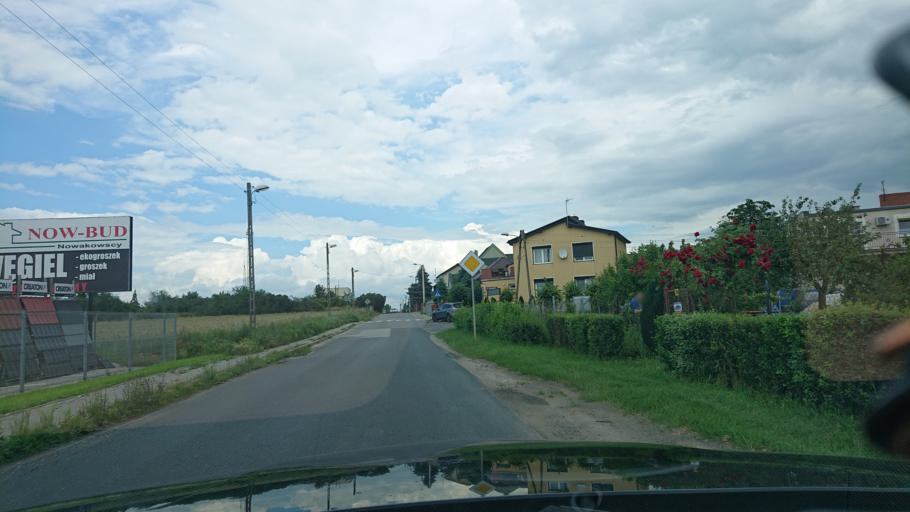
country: PL
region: Greater Poland Voivodeship
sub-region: Powiat gnieznienski
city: Gniezno
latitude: 52.5381
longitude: 17.6340
